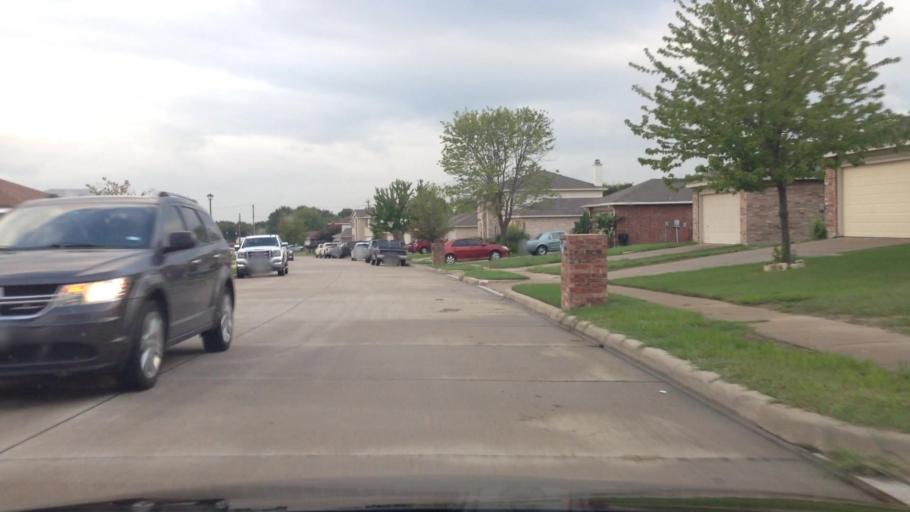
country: US
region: Texas
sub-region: Tarrant County
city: Crowley
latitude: 32.5636
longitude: -97.3404
